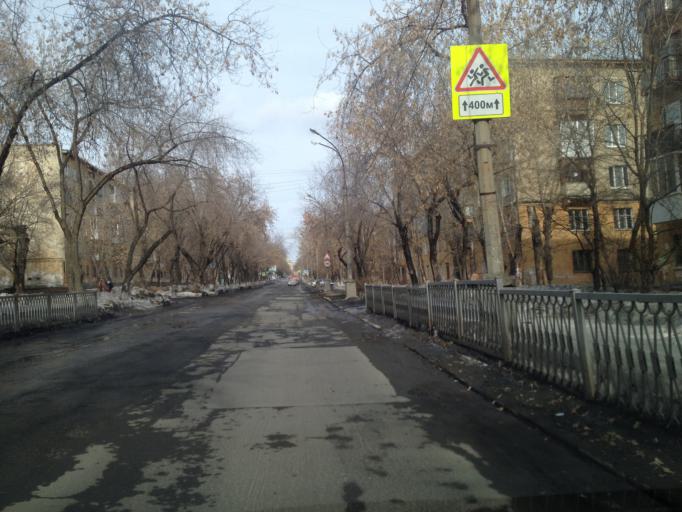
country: RU
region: Sverdlovsk
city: Sovkhoznyy
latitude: 56.7724
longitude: 60.6086
